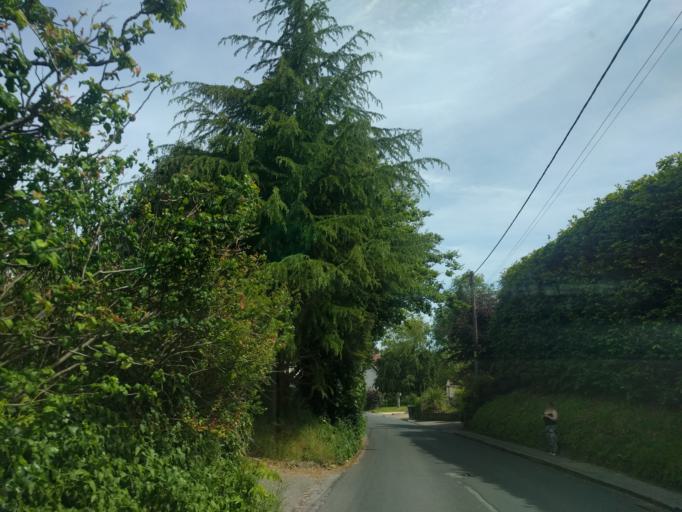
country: GB
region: England
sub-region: Wiltshire
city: Erlestoke
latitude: 51.2830
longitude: -2.0561
